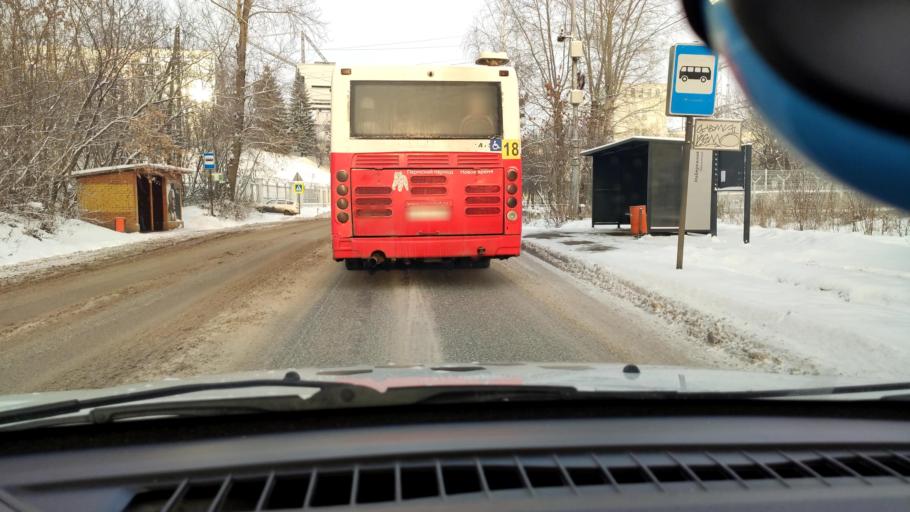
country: RU
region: Perm
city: Perm
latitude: 58.1130
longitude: 56.3245
